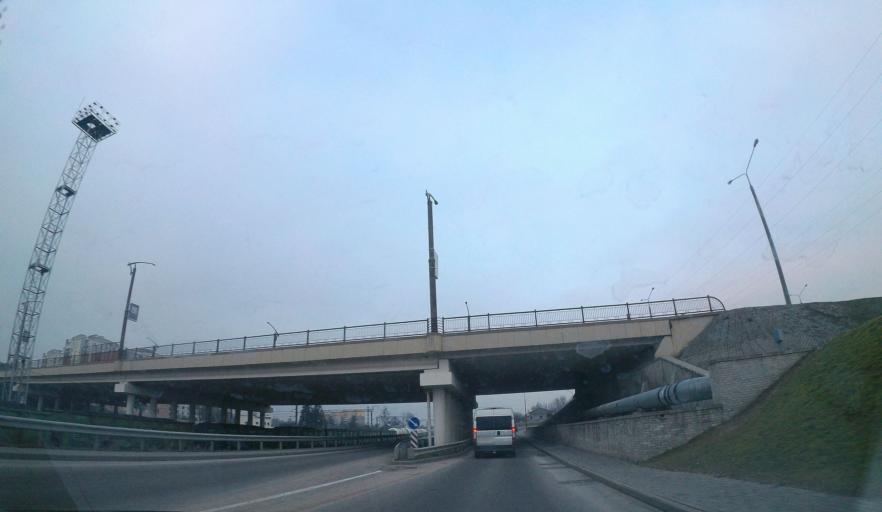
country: BY
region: Grodnenskaya
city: Hrodna
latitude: 53.6499
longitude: 23.8013
